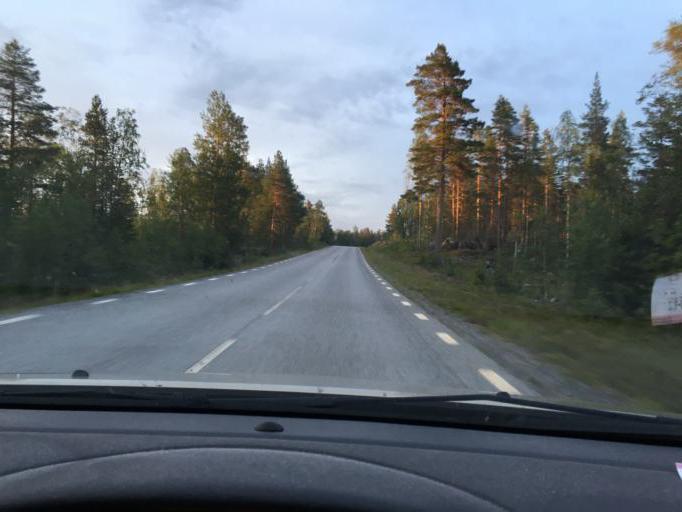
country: SE
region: Norrbotten
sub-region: Lulea Kommun
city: Ranea
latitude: 66.0544
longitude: 22.4341
